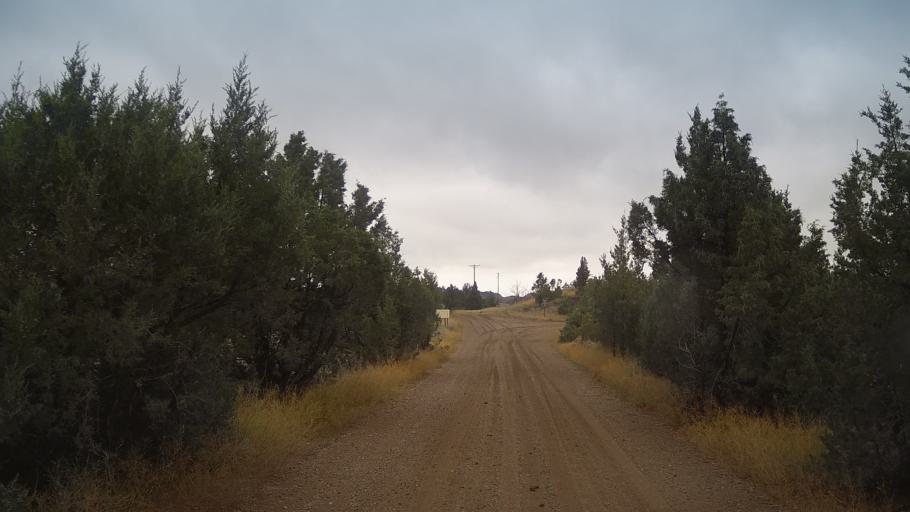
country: US
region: Montana
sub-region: Dawson County
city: Glendive
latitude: 47.0446
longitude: -104.6767
